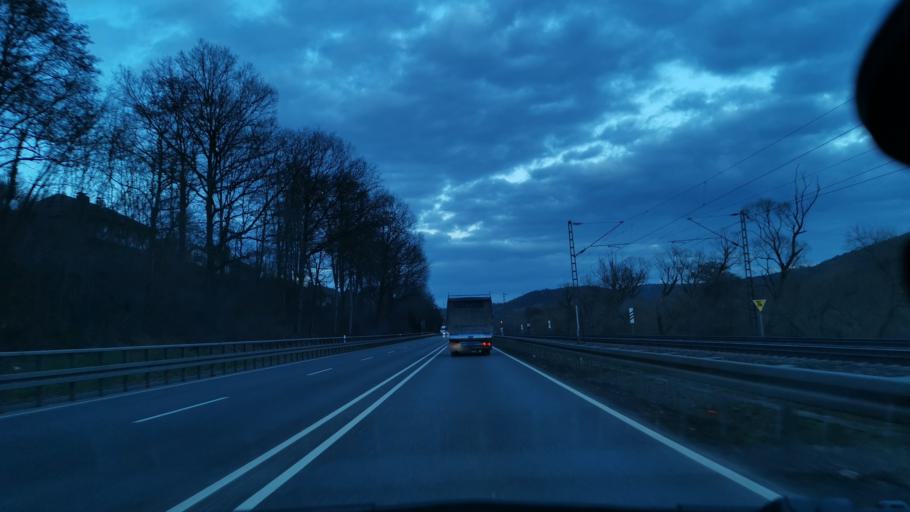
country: DE
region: Hesse
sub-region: Regierungsbezirk Kassel
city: Bad Hersfeld
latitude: 50.8924
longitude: 9.7343
